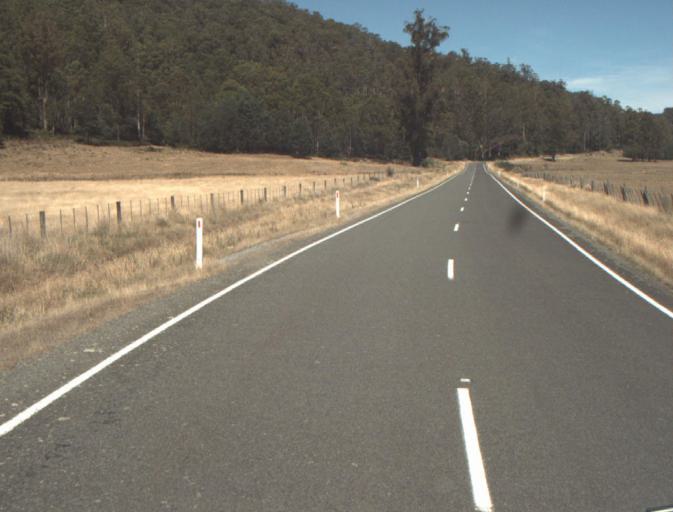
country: AU
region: Tasmania
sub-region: Dorset
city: Scottsdale
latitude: -41.2929
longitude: 147.3854
